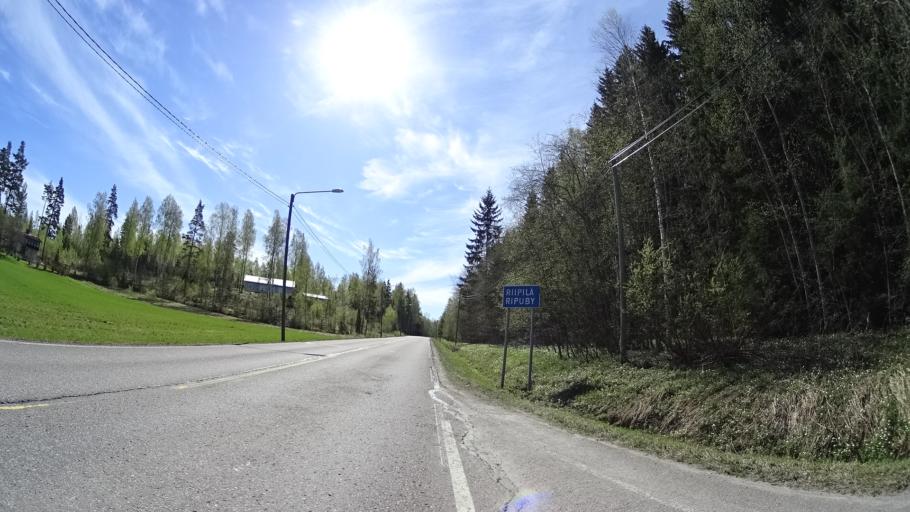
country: FI
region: Uusimaa
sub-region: Helsinki
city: Nurmijaervi
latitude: 60.3923
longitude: 24.8339
